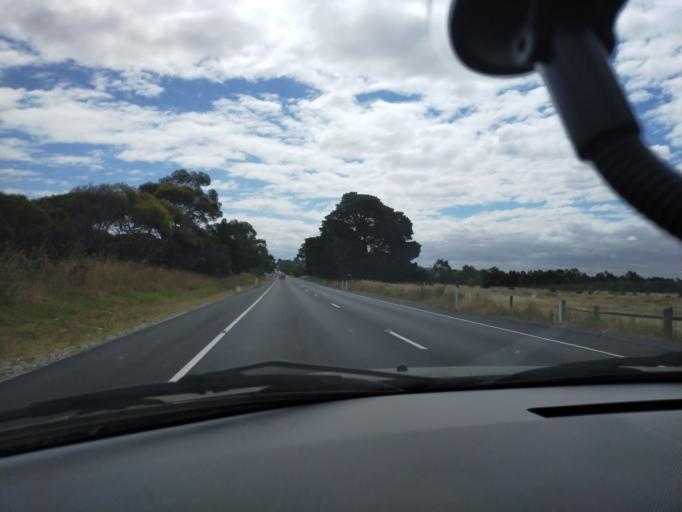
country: AU
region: Victoria
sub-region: Greater Geelong
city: Breakwater
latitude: -38.2510
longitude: 144.3539
